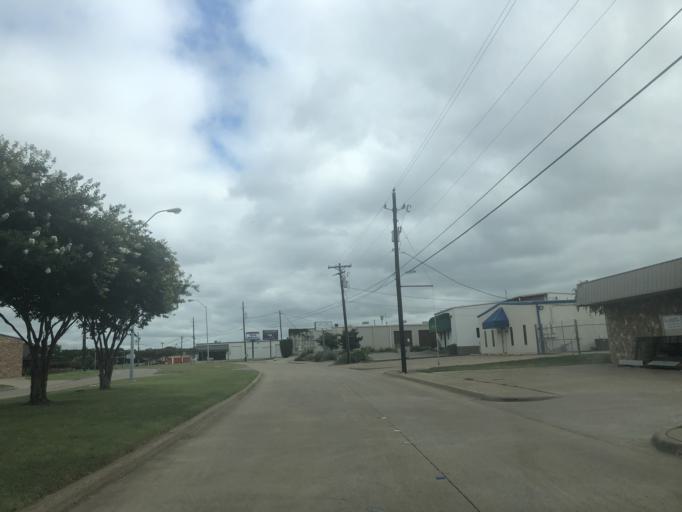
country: US
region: Texas
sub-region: Dallas County
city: Duncanville
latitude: 32.6386
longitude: -96.9242
